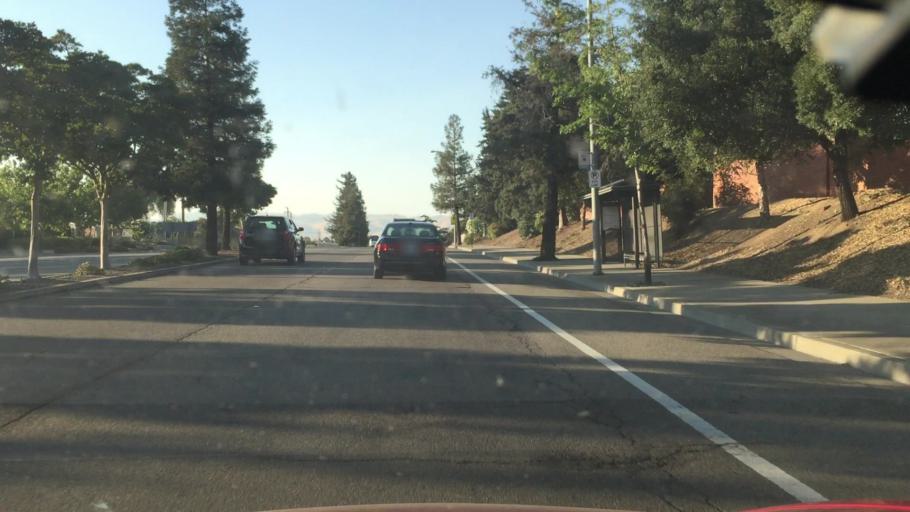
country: US
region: California
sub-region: Alameda County
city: Livermore
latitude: 37.6938
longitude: -121.7731
